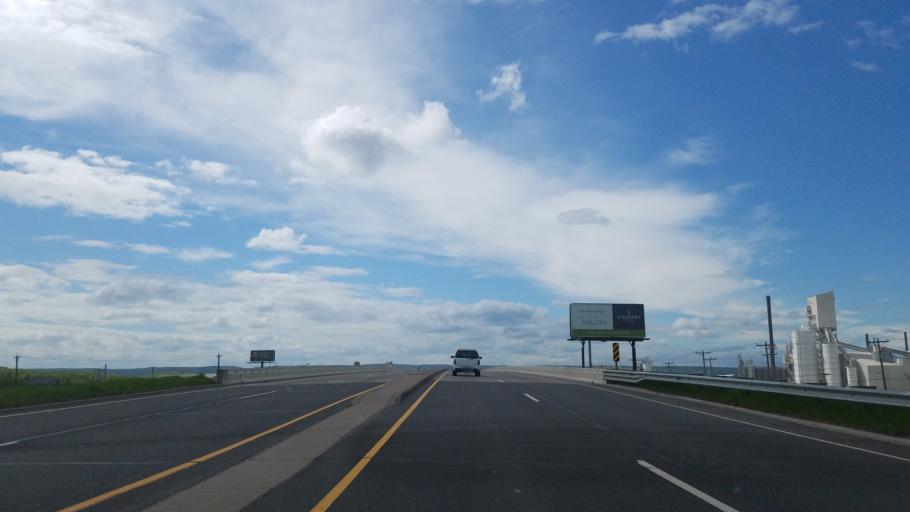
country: US
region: Wisconsin
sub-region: Douglas County
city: Superior
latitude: 46.7267
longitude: -92.0751
